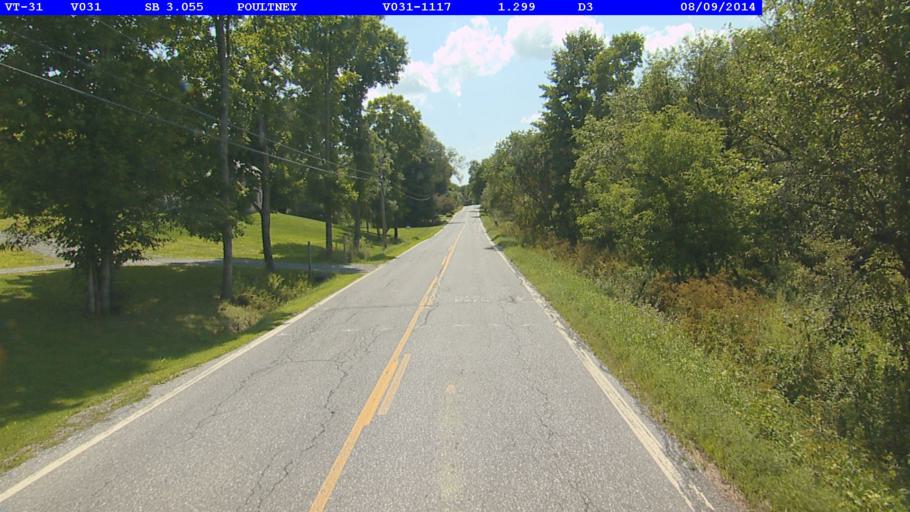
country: US
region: Vermont
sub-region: Rutland County
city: Poultney
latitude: 43.4806
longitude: -73.2420
